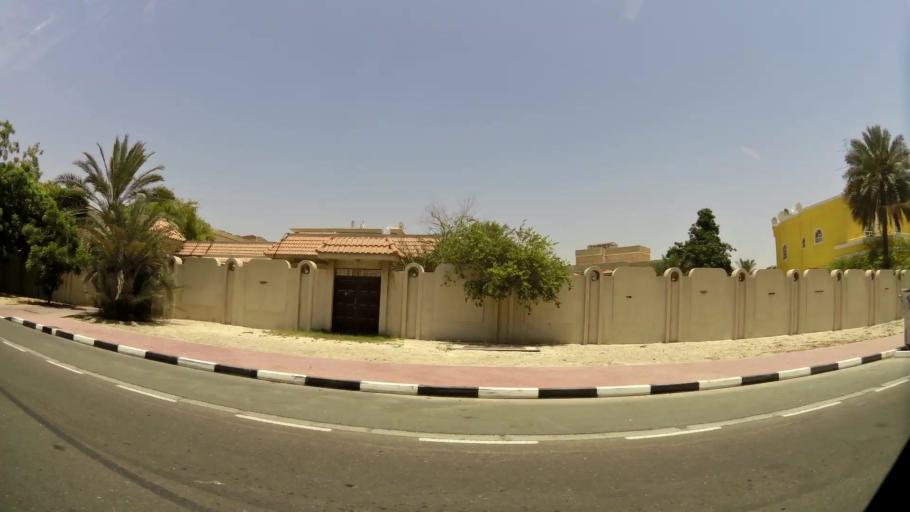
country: AE
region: Ash Shariqah
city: Sharjah
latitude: 25.2393
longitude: 55.2899
